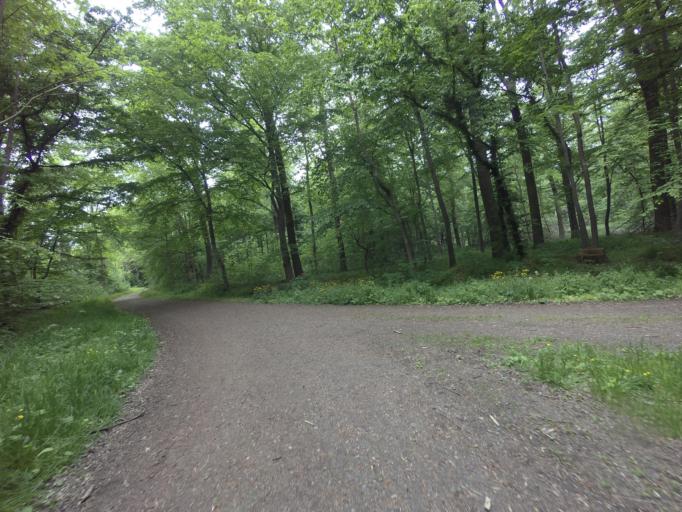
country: DE
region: Lower Saxony
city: Cremlingen
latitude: 52.2578
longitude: 10.5990
